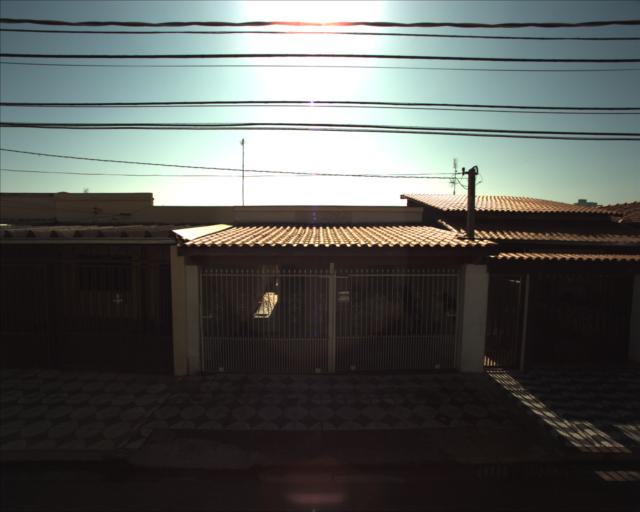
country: BR
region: Sao Paulo
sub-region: Sorocaba
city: Sorocaba
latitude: -23.5089
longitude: -47.4346
